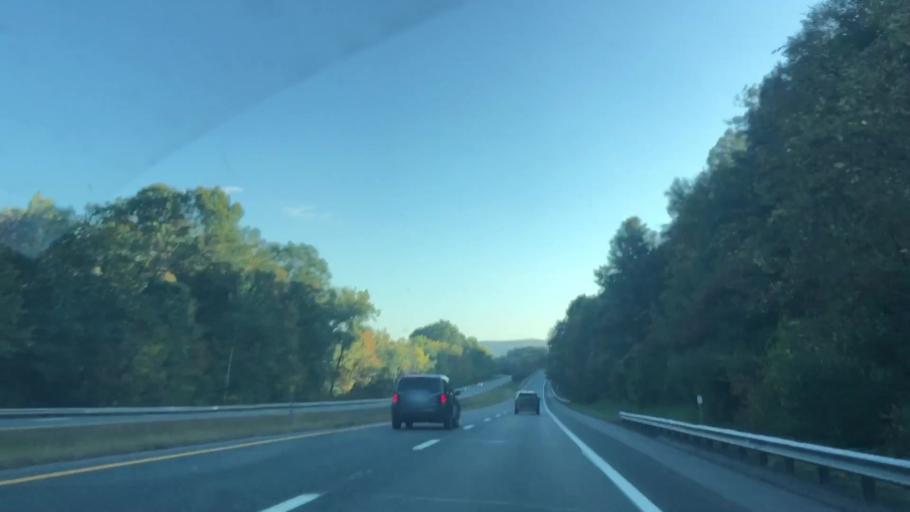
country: US
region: New Hampshire
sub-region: Cheshire County
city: Chesterfield
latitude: 42.9372
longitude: -72.5275
